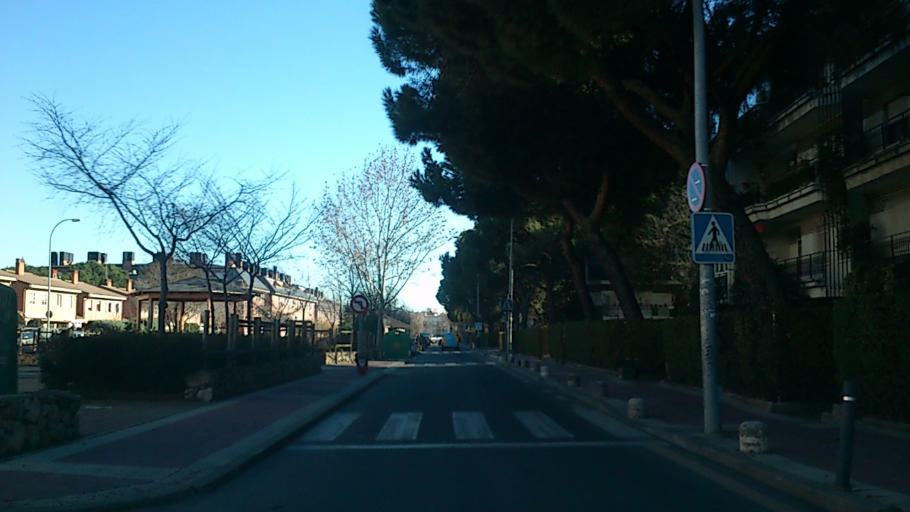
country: ES
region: Madrid
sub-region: Provincia de Madrid
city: Collado-Villalba
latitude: 40.6358
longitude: -4.0169
